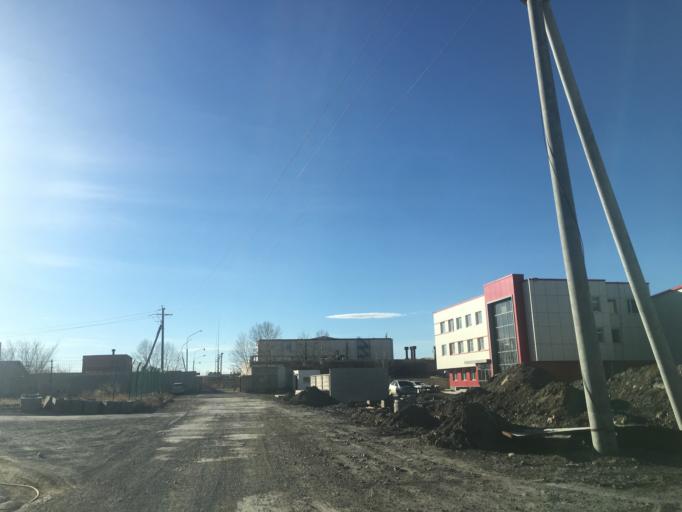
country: MN
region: Ulaanbaatar
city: Ulaanbaatar
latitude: 47.8987
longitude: 106.7959
